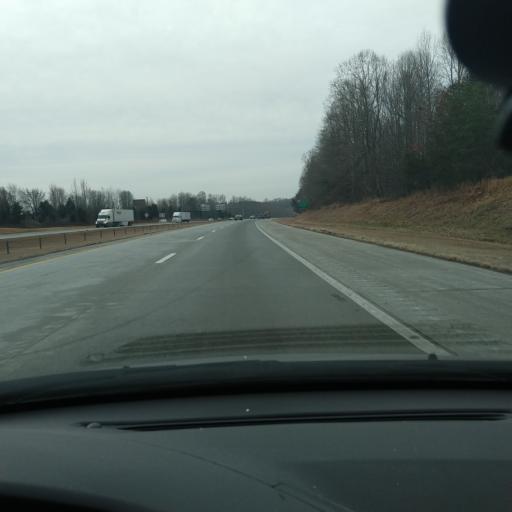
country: US
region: North Carolina
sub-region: Davidson County
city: Lexington
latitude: 35.8153
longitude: -80.2854
